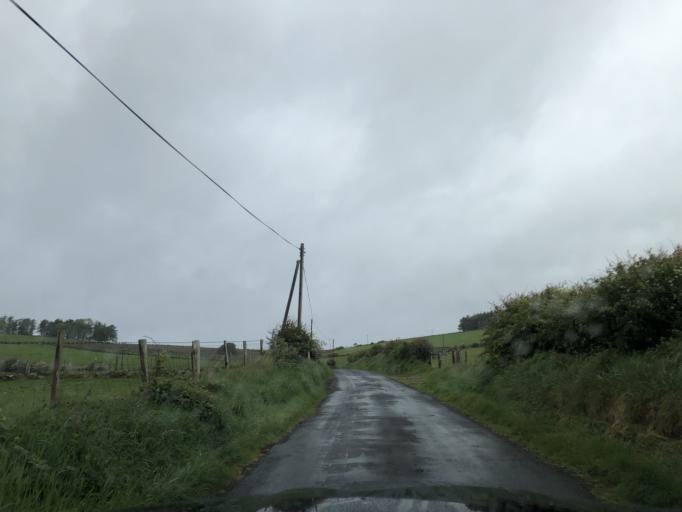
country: GB
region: Northern Ireland
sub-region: Moyle District
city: Ballycastle
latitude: 55.2033
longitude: -6.1722
